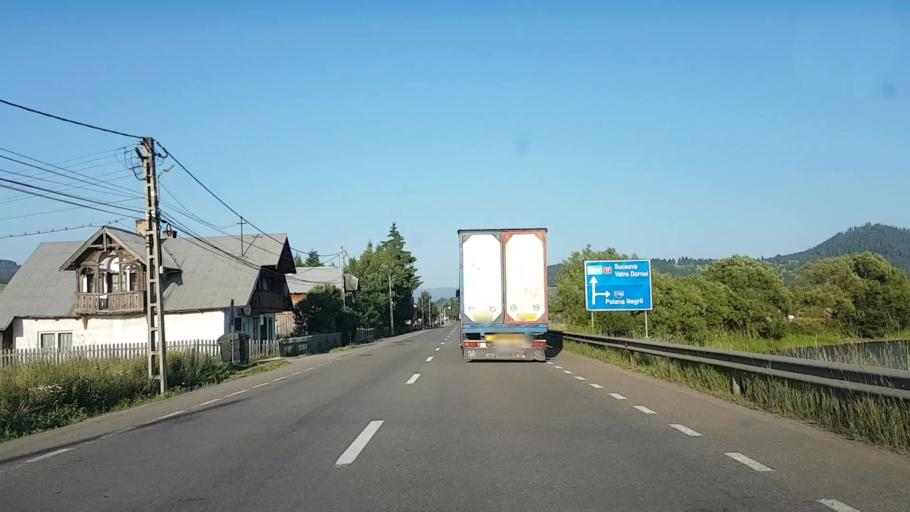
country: RO
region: Suceava
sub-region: Comuna Dorna Candrenilor
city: Dorna Candrenilor
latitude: 47.3565
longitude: 25.2387
